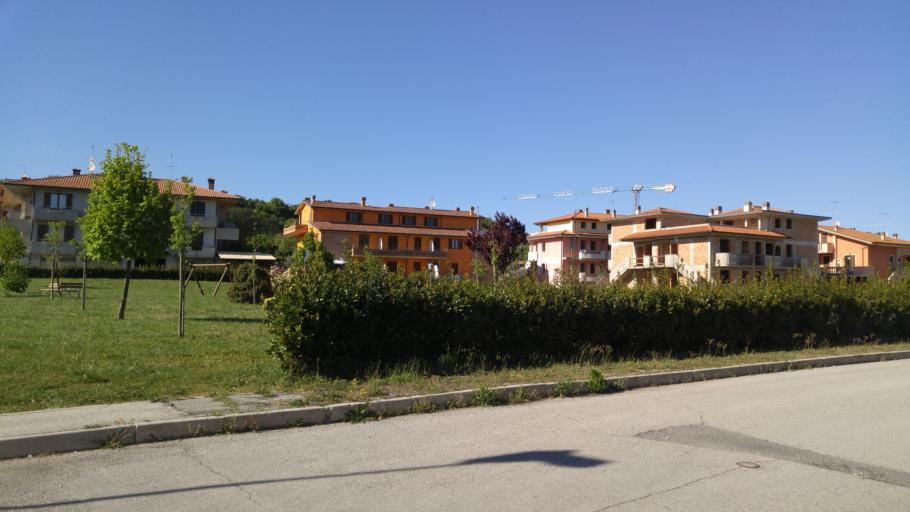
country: IT
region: The Marches
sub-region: Provincia di Pesaro e Urbino
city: Saltara
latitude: 43.7371
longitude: 12.8994
